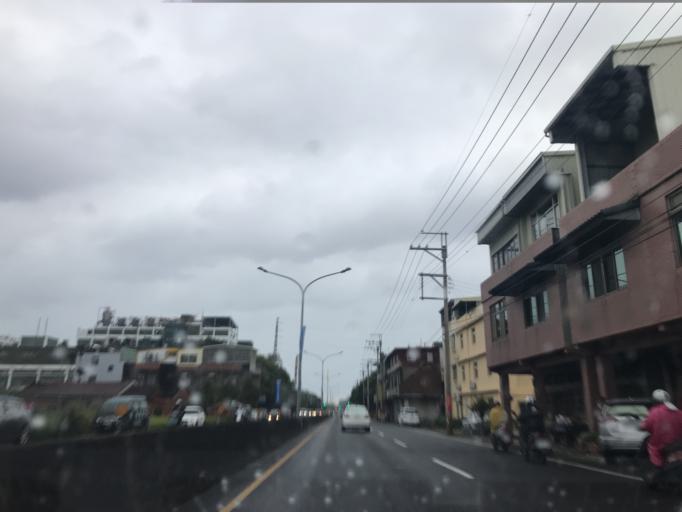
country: TW
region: Taiwan
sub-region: Hsinchu
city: Zhubei
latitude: 24.8247
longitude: 121.0607
